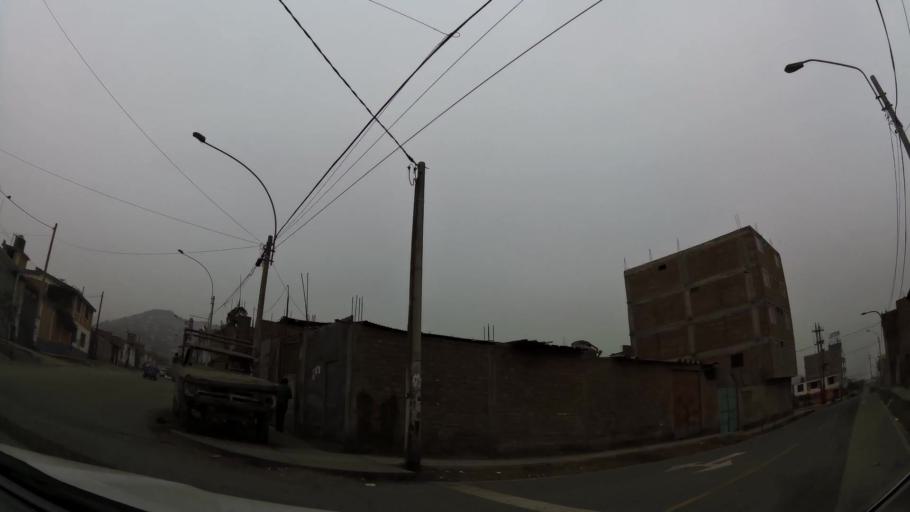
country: PE
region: Lima
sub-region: Lima
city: Urb. Santo Domingo
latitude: -11.9342
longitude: -76.9676
